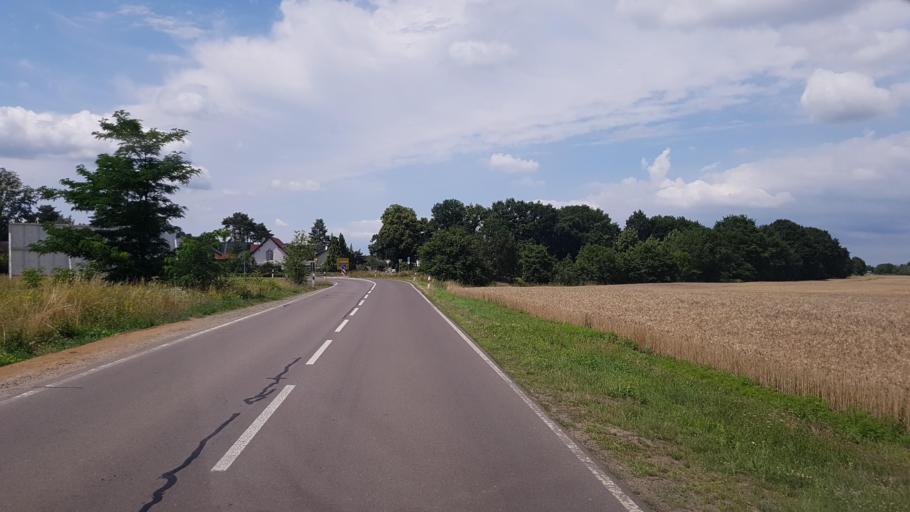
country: DE
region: Brandenburg
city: Senftenberg
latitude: 51.4927
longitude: 14.0705
